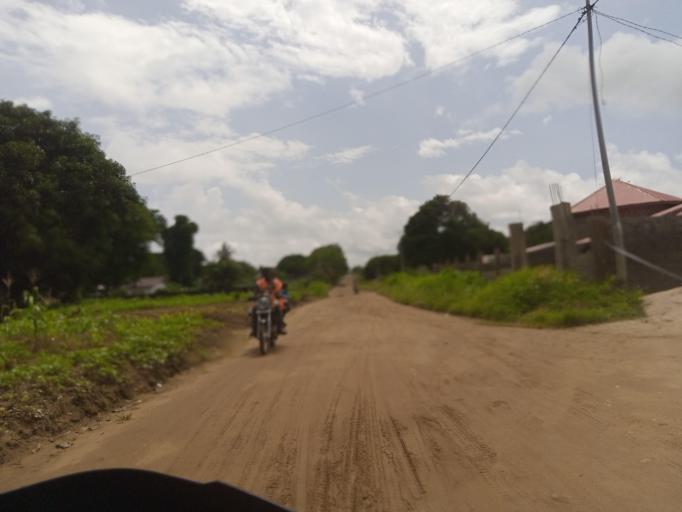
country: SL
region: Northern Province
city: Tintafor
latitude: 8.6254
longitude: -13.2087
